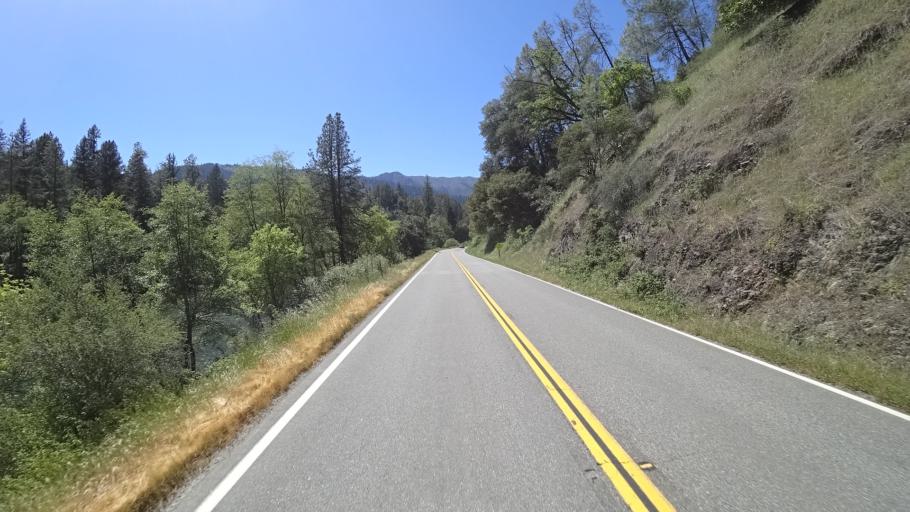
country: US
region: California
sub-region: Trinity County
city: Hayfork
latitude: 40.7393
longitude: -123.2482
